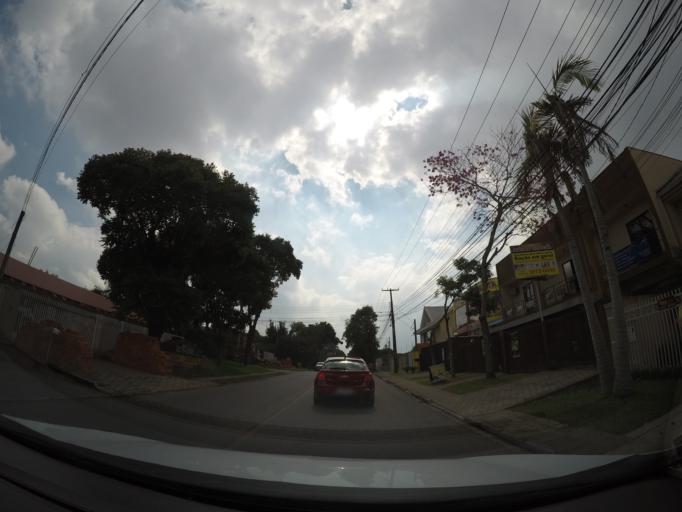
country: BR
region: Parana
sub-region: Sao Jose Dos Pinhais
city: Sao Jose dos Pinhais
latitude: -25.5007
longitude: -49.2504
